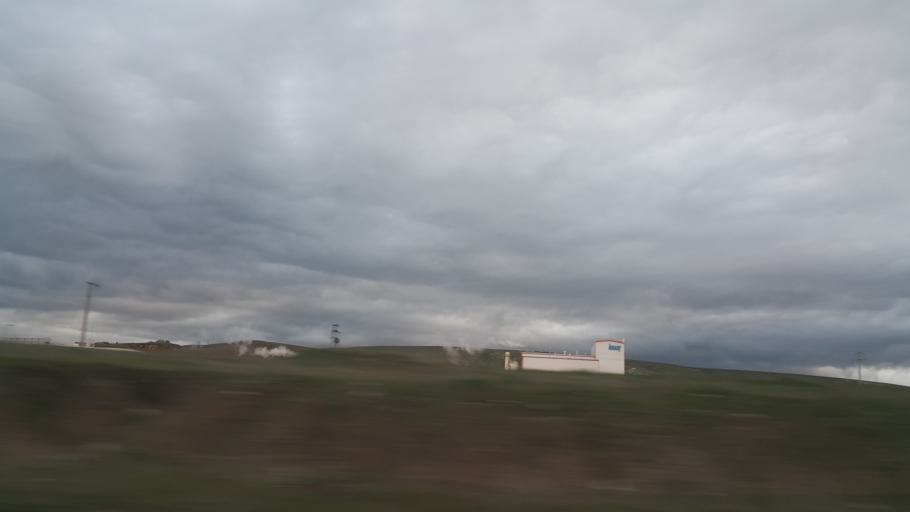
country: TR
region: Ankara
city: Ikizce
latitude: 39.5855
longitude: 32.8535
